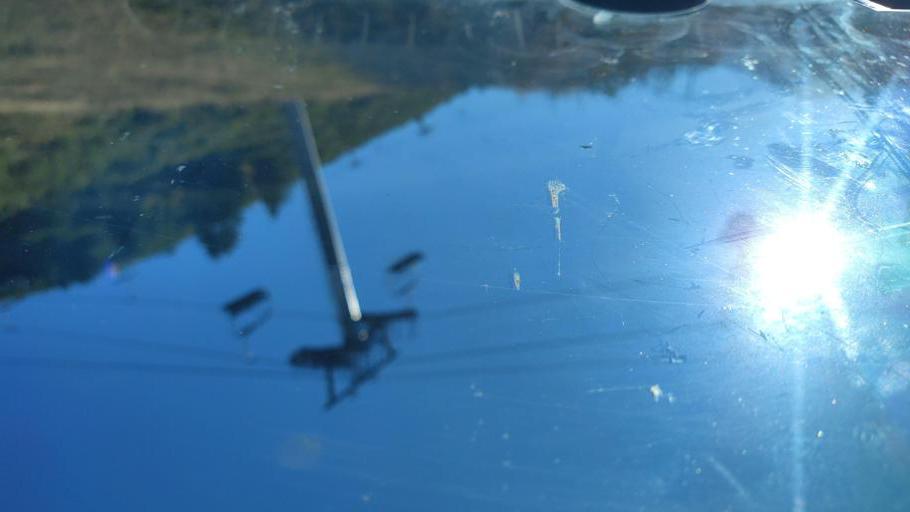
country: FR
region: Rhone-Alpes
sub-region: Departement de la Savoie
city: Valloire
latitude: 45.1724
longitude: 6.4707
